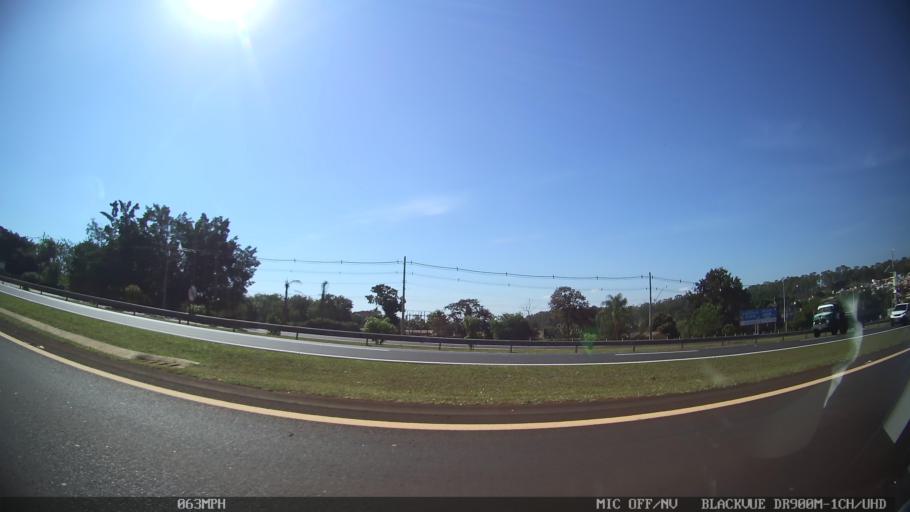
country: BR
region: Sao Paulo
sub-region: Ribeirao Preto
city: Ribeirao Preto
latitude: -21.2149
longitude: -47.8388
